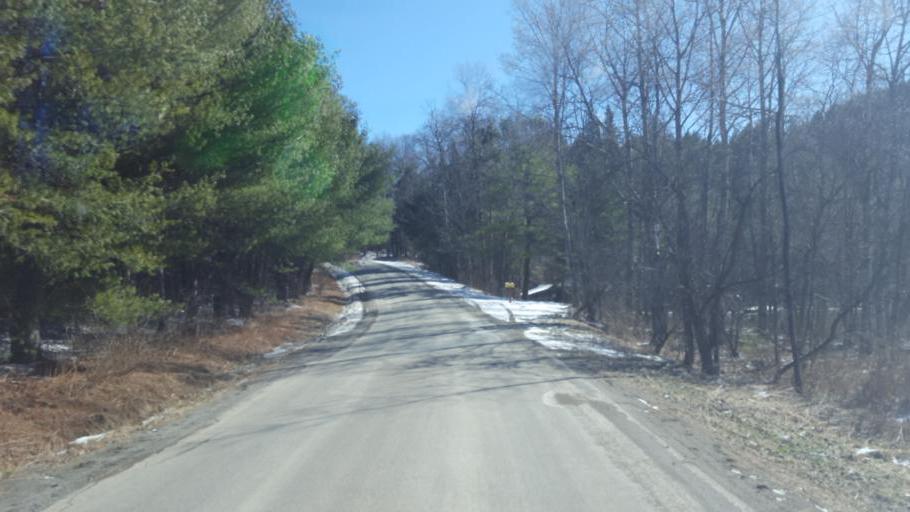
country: US
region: New York
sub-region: Allegany County
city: Wellsville
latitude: 42.0718
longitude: -77.9419
